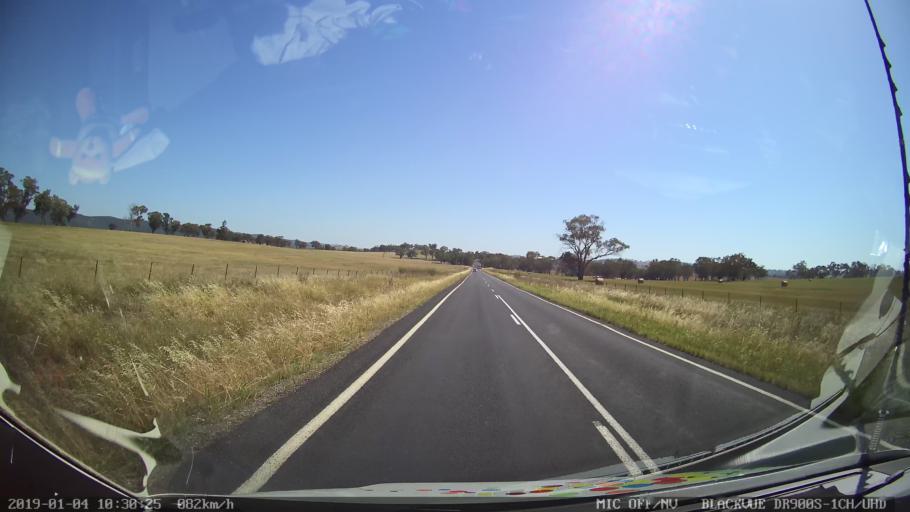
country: AU
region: New South Wales
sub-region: Cabonne
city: Canowindra
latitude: -33.3460
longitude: 148.6277
